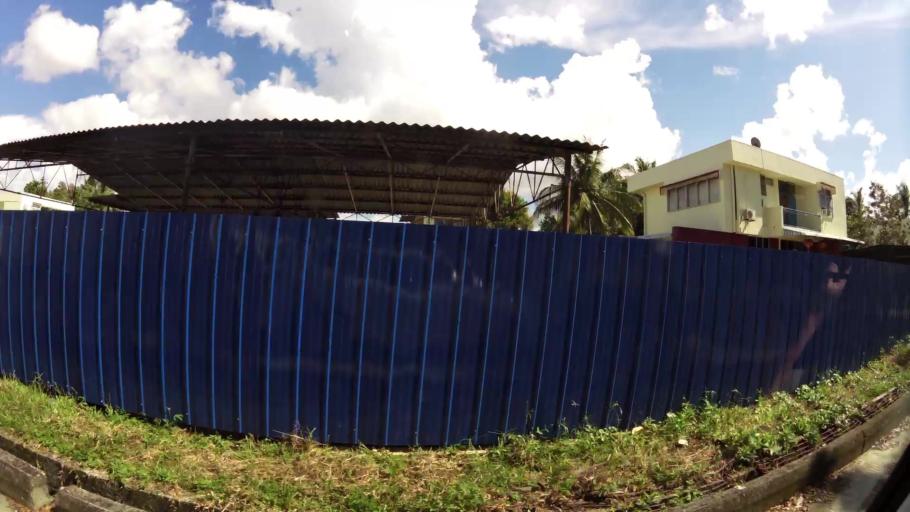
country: BN
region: Brunei and Muara
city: Bandar Seri Begawan
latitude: 4.9561
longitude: 114.9434
